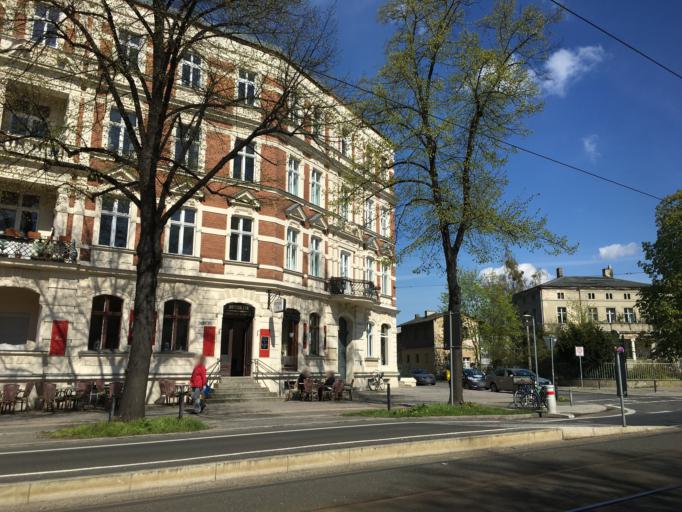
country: DE
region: Brandenburg
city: Potsdam
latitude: 52.4079
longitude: 13.0757
